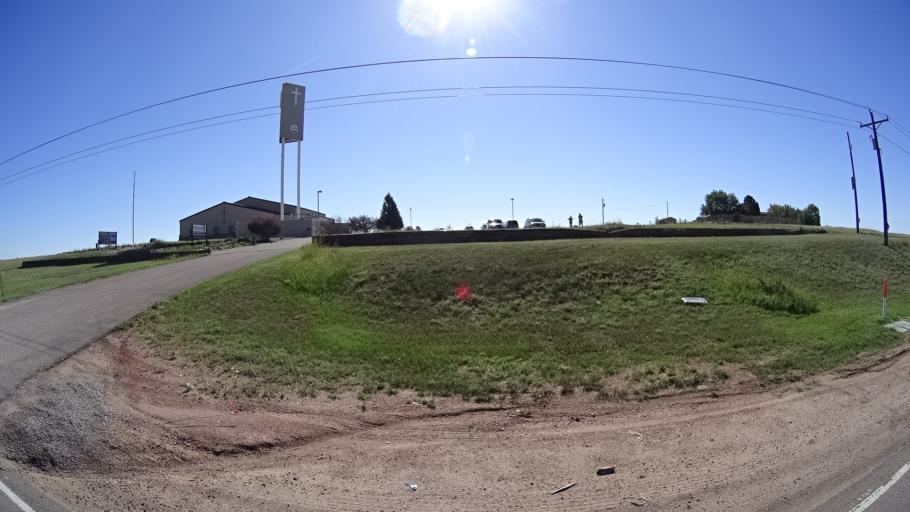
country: US
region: Colorado
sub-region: El Paso County
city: Cimarron Hills
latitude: 38.9130
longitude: -104.6829
